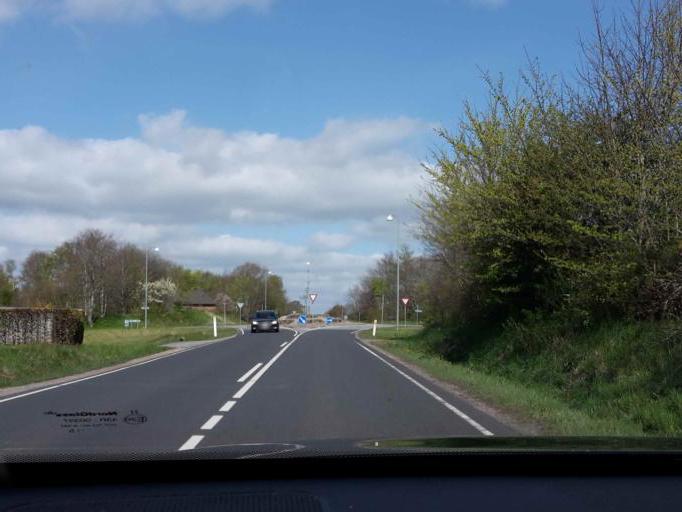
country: DK
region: South Denmark
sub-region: Varde Kommune
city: Olgod
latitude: 55.7081
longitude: 8.7539
